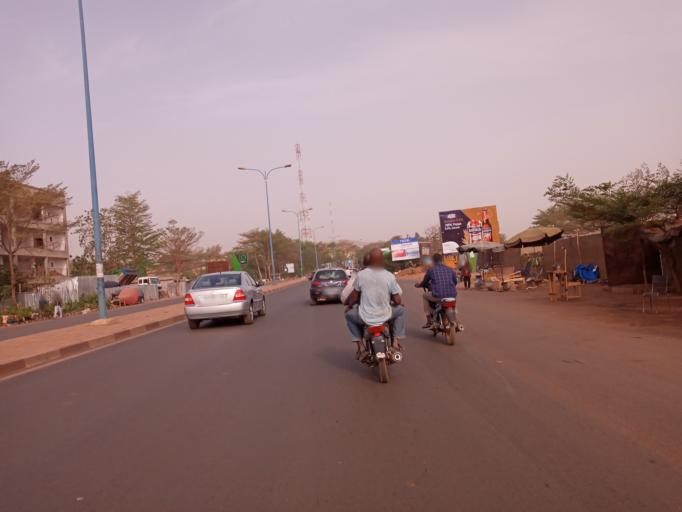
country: ML
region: Bamako
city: Bamako
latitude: 12.6378
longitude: -8.0179
